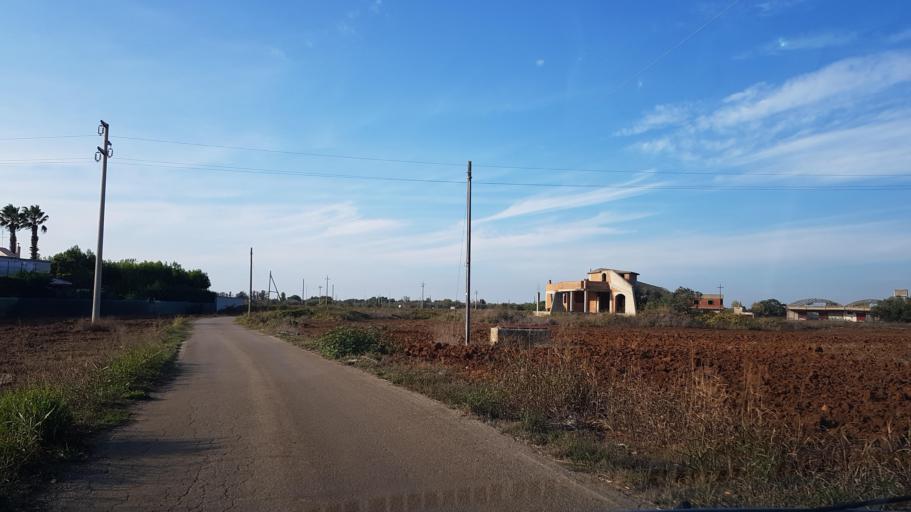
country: IT
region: Apulia
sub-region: Provincia di Brindisi
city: Mesagne
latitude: 40.5402
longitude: 17.8259
